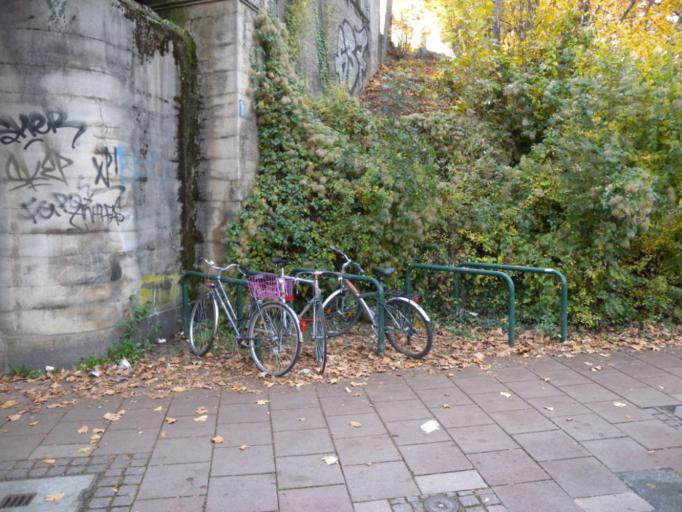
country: DE
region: Baden-Wuerttemberg
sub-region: Regierungsbezirk Stuttgart
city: Stuttgart
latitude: 48.8036
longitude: 9.1895
